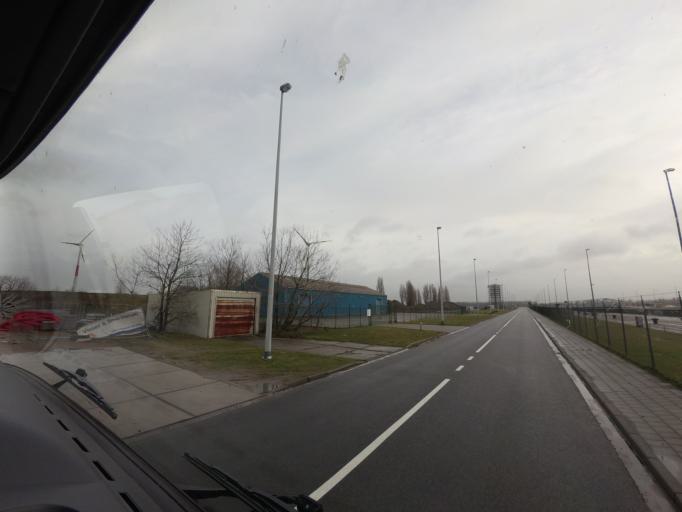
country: NL
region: North Brabant
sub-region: Gemeente Woensdrecht
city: Woensdrecht
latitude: 51.3468
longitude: 4.2844
